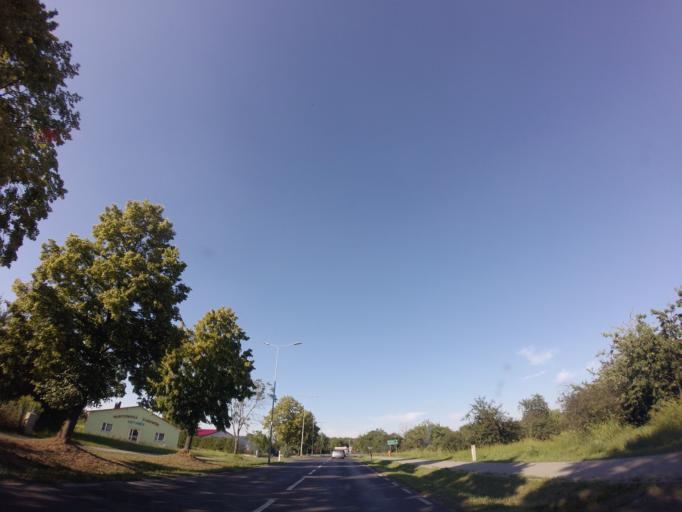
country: PL
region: Lubusz
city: Gorzow Wielkopolski
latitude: 52.7478
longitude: 15.2880
